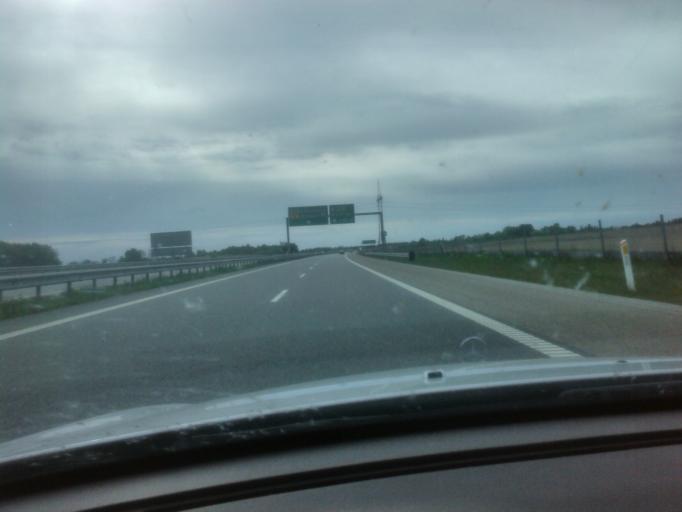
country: DK
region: South Denmark
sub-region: Aabenraa Kommune
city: Krusa
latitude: 54.9443
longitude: 9.3973
